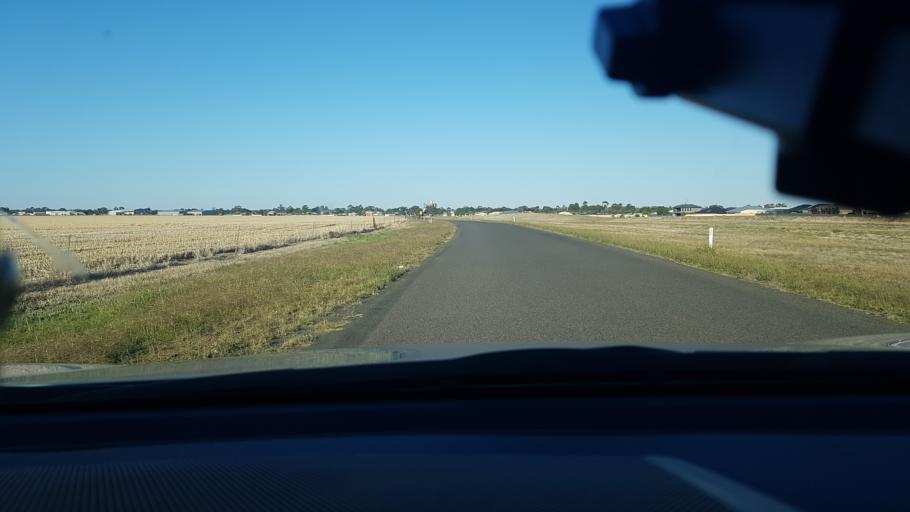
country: AU
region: Victoria
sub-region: Horsham
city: Horsham
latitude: -36.7132
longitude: 142.1721
